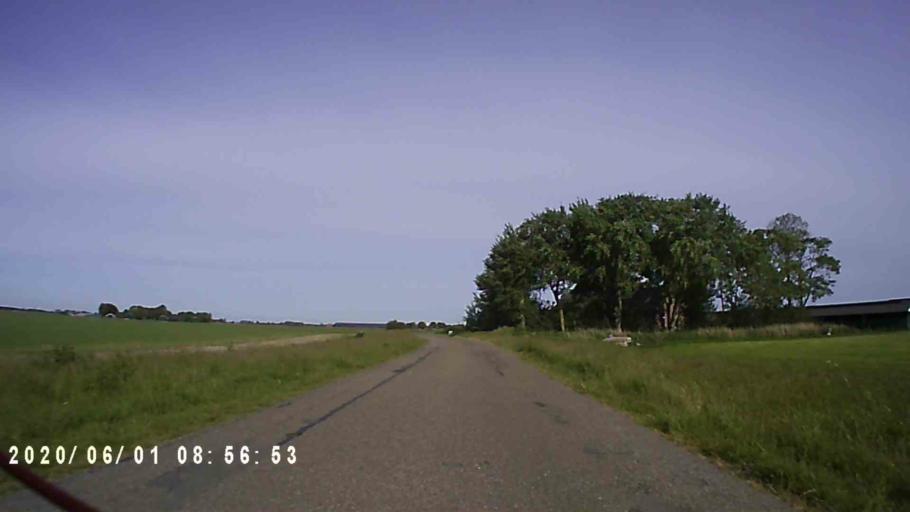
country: NL
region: Friesland
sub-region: Gemeente Leeuwarderadeel
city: Britsum
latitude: 53.2800
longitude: 5.8162
